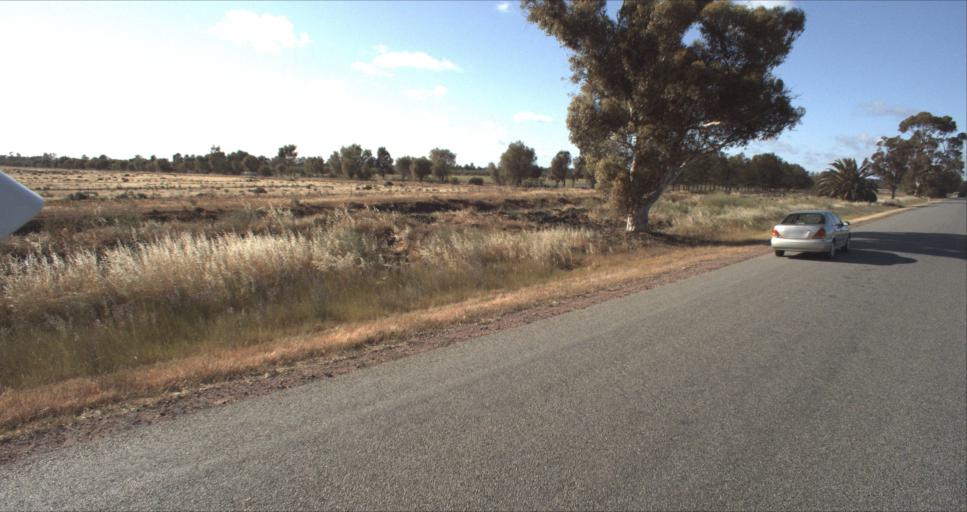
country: AU
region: New South Wales
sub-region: Leeton
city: Leeton
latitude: -34.5181
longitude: 146.3911
